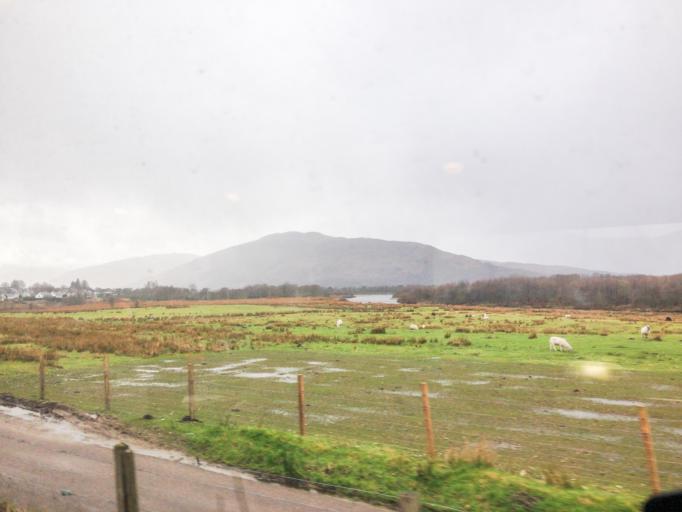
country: GB
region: Scotland
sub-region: Highland
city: Fort William
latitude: 56.8312
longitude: -5.0839
